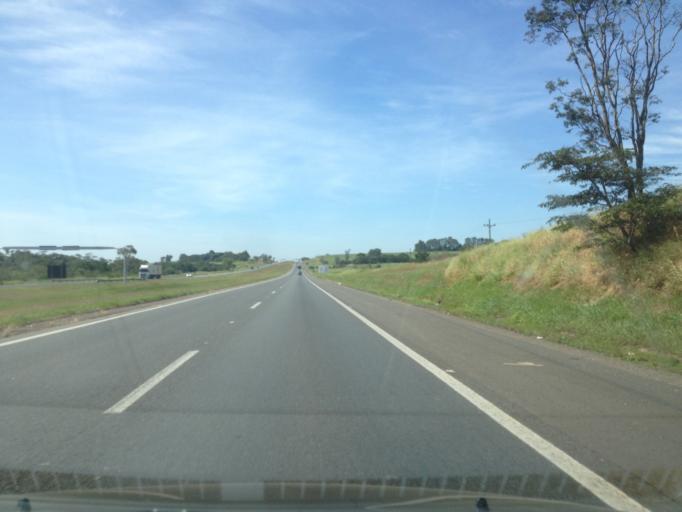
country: BR
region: Sao Paulo
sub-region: Tatui
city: Tatui
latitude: -23.2552
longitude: -47.9201
